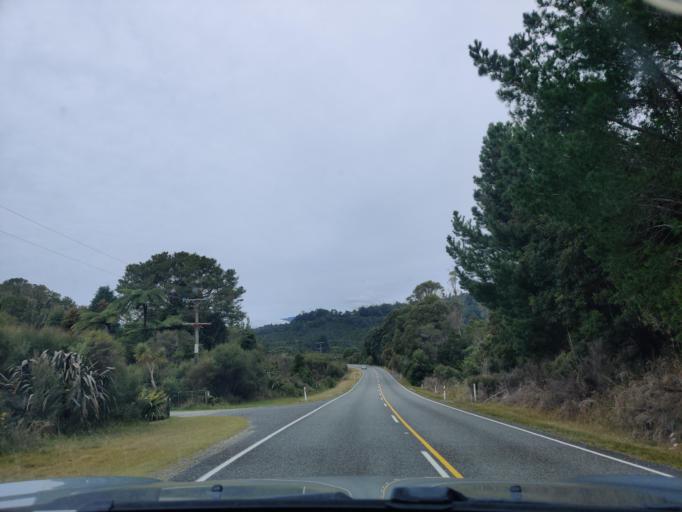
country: NZ
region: West Coast
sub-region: Buller District
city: Westport
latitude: -41.8941
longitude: 171.4568
